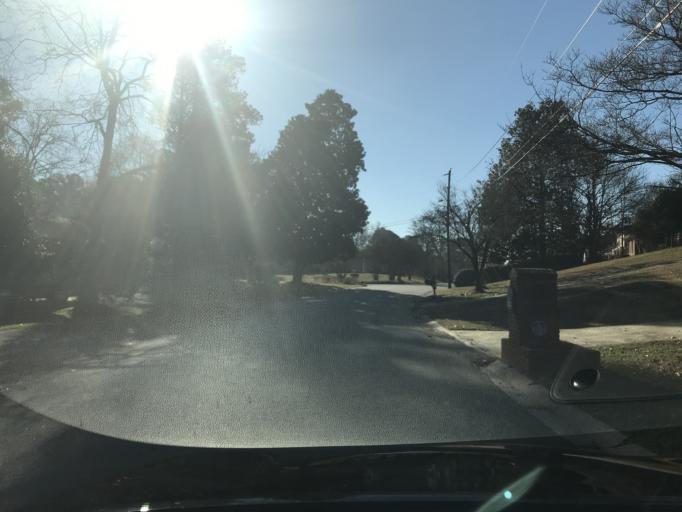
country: US
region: Georgia
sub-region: Clayton County
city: Morrow
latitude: 33.5659
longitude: -84.3684
